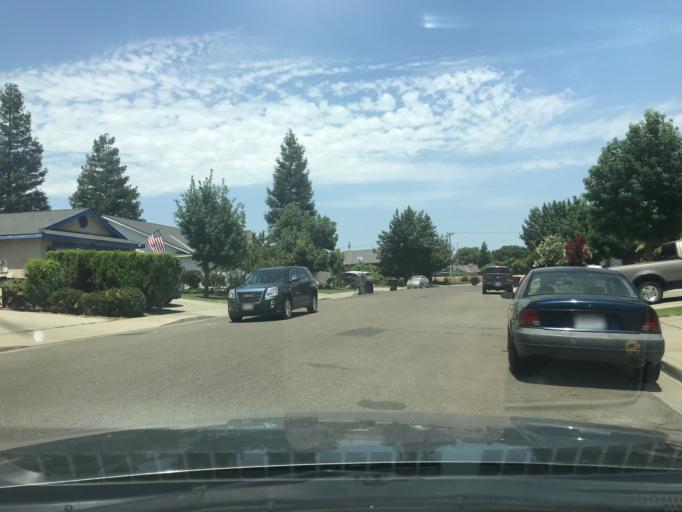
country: US
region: California
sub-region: Merced County
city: Atwater
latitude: 37.3625
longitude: -120.5980
